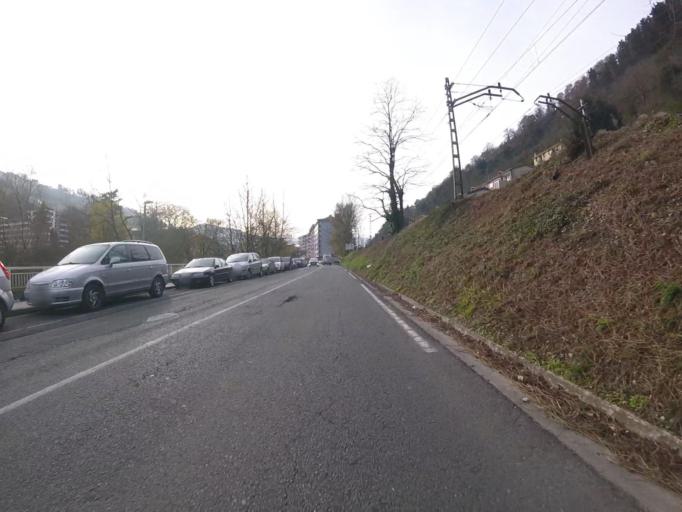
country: ES
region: Basque Country
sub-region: Provincia de Guipuzcoa
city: Tolosa
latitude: 43.1441
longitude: -2.0728
